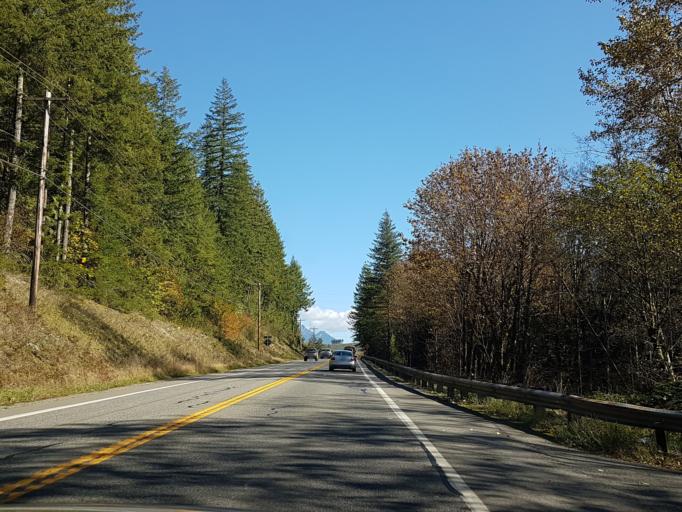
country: US
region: Washington
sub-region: Snohomish County
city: Gold Bar
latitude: 47.8395
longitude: -121.6632
